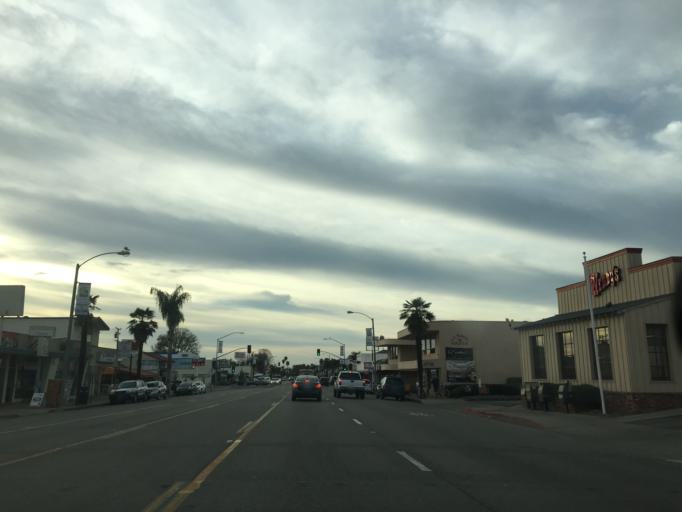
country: US
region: California
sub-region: Santa Barbara County
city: Goleta
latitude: 34.4357
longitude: -119.8238
